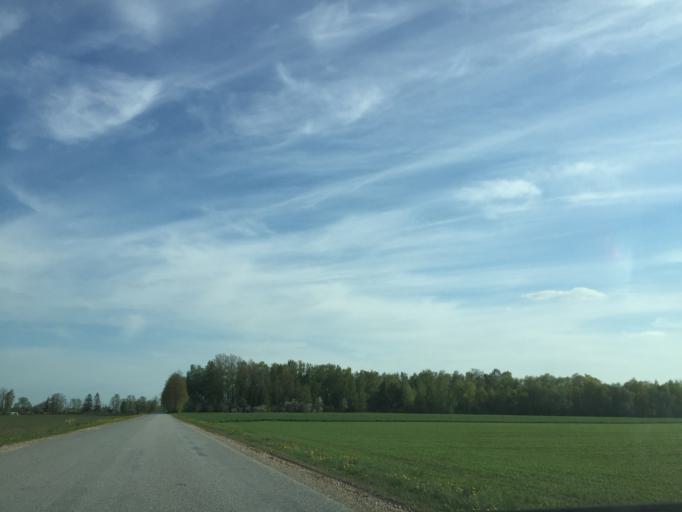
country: LV
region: Bauskas Rajons
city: Bauska
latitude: 56.3487
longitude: 24.2334
